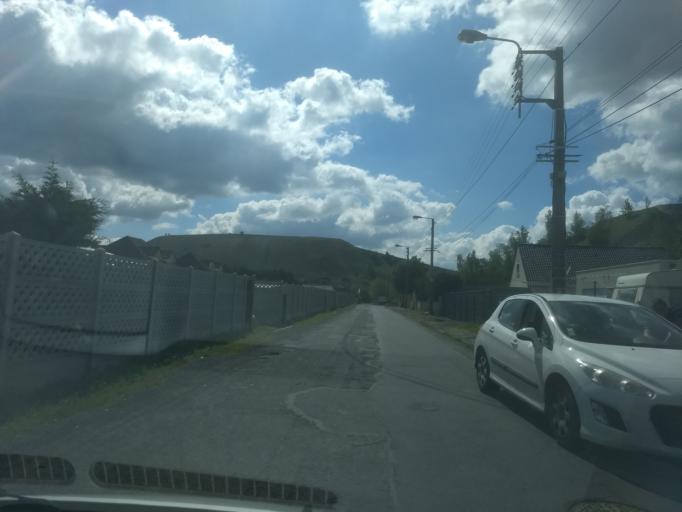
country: FR
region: Nord-Pas-de-Calais
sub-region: Departement du Pas-de-Calais
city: Drocourt
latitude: 50.4093
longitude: 2.9276
